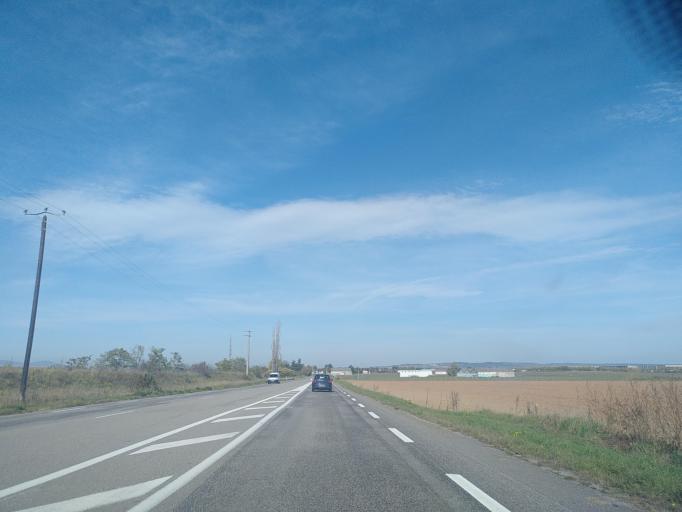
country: FR
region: Rhone-Alpes
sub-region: Departement de la Drome
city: Andancette
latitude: 45.2492
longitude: 4.8215
